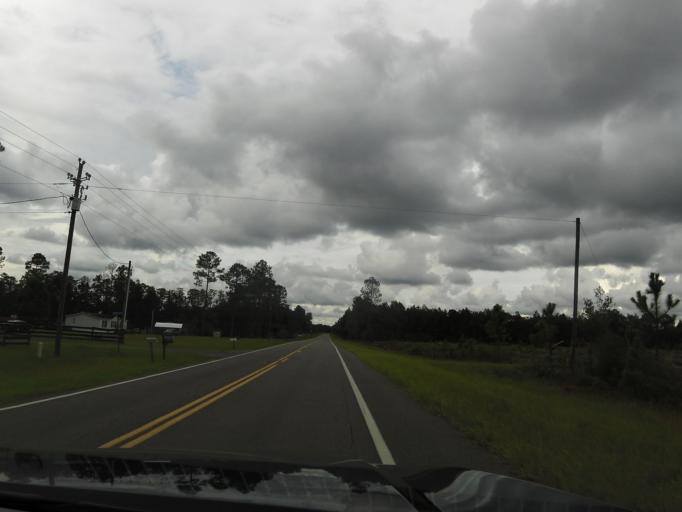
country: US
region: Florida
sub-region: Baker County
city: Macclenny
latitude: 30.4728
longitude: -82.1980
